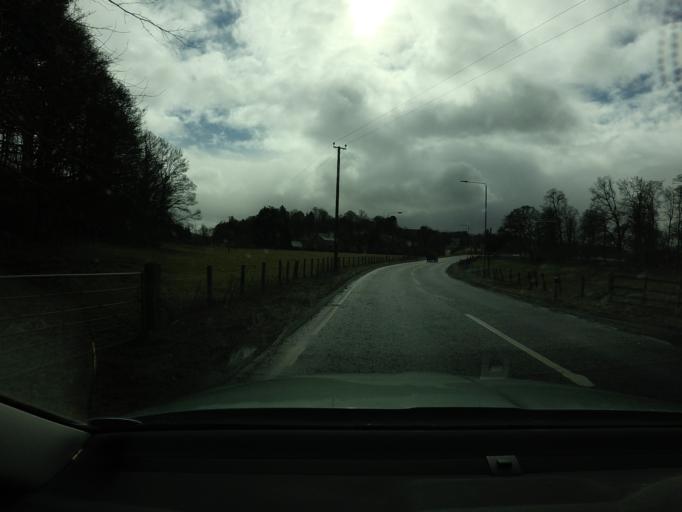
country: GB
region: Scotland
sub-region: South Lanarkshire
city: Douglas
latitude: 55.5785
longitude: -3.8085
